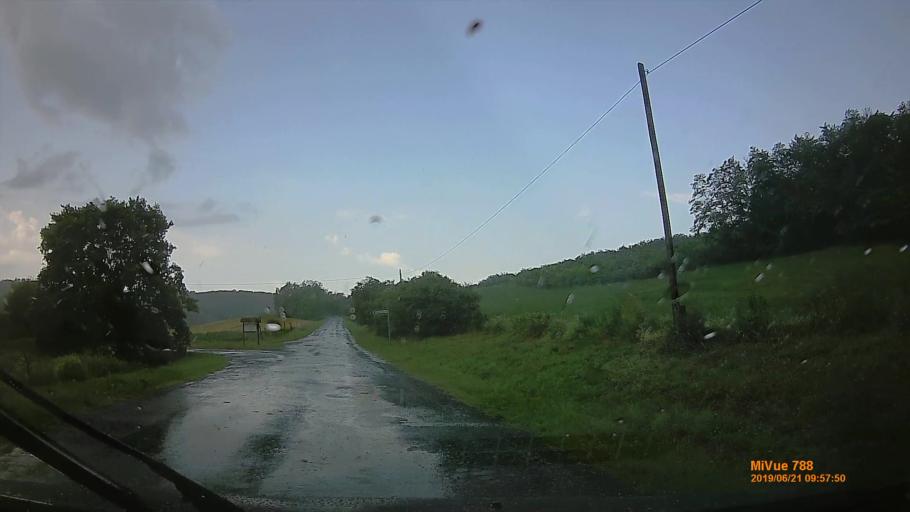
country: HU
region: Baranya
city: Buekkoesd
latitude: 46.2183
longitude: 17.9706
